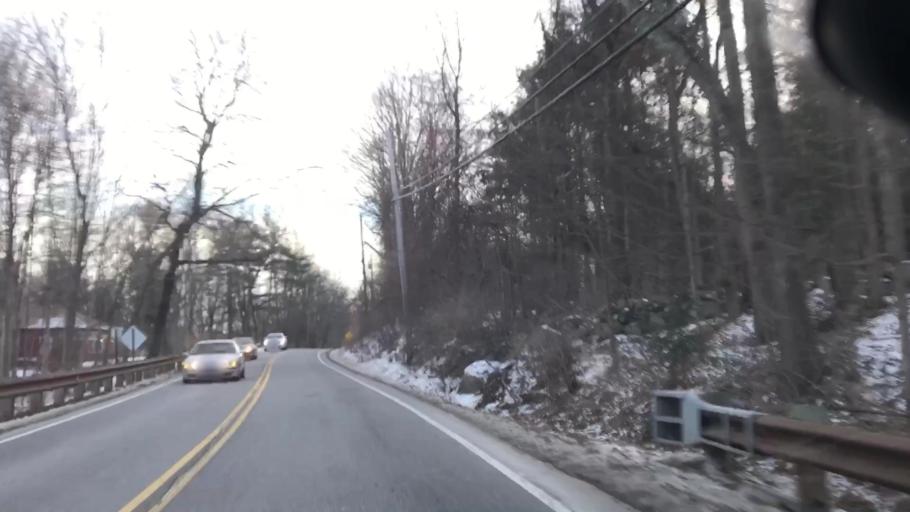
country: US
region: New Hampshire
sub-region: Hillsborough County
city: Bedford
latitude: 42.9421
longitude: -71.5276
